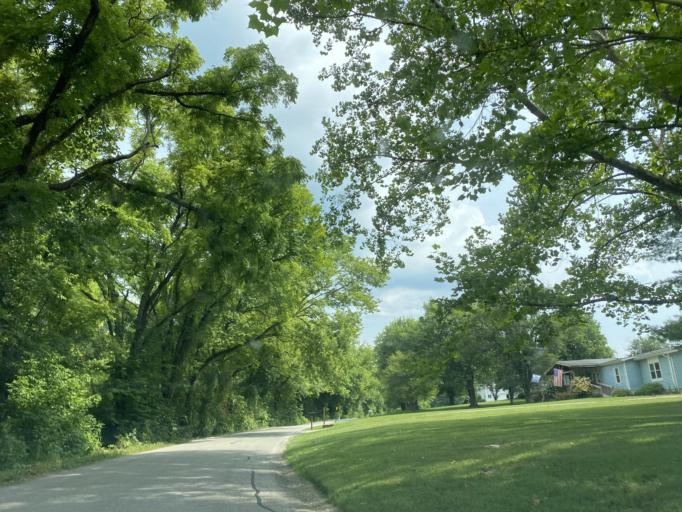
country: US
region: Kentucky
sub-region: Pendleton County
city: Falmouth
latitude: 38.7996
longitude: -84.3270
